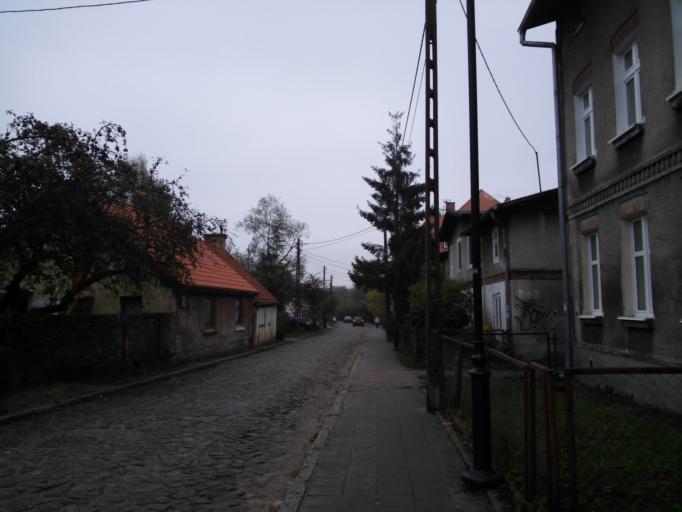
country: PL
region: Pomeranian Voivodeship
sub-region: Sopot
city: Sopot
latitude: 54.4081
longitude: 18.5520
